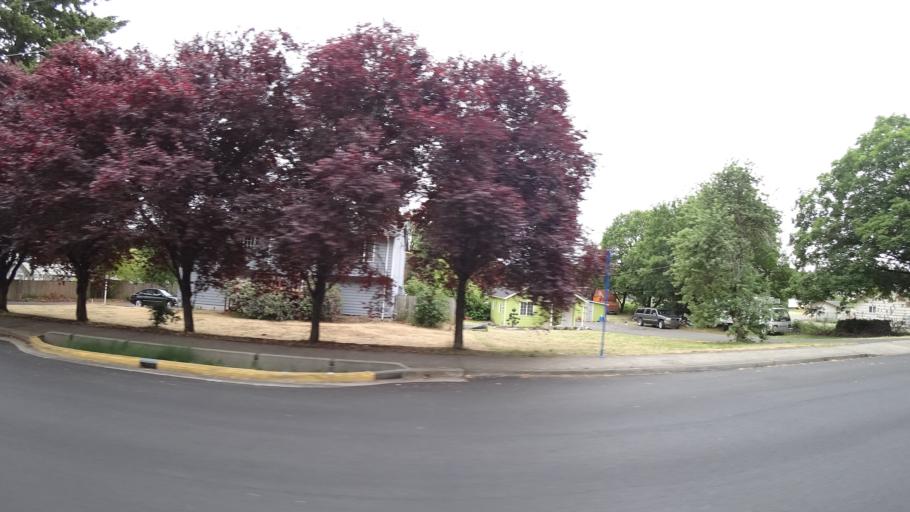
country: US
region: Oregon
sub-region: Multnomah County
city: Lents
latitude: 45.4897
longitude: -122.5295
